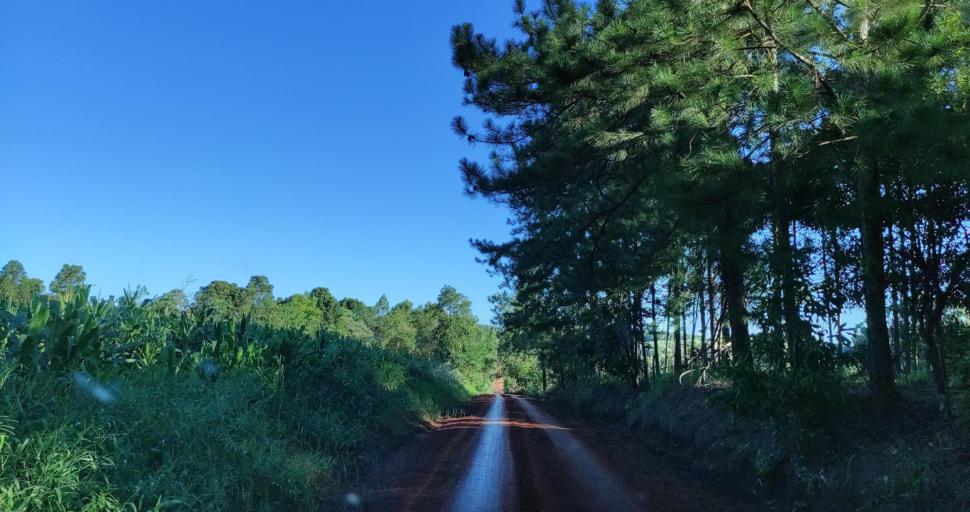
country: AR
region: Misiones
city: Puerto Rico
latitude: -26.8459
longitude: -55.0132
